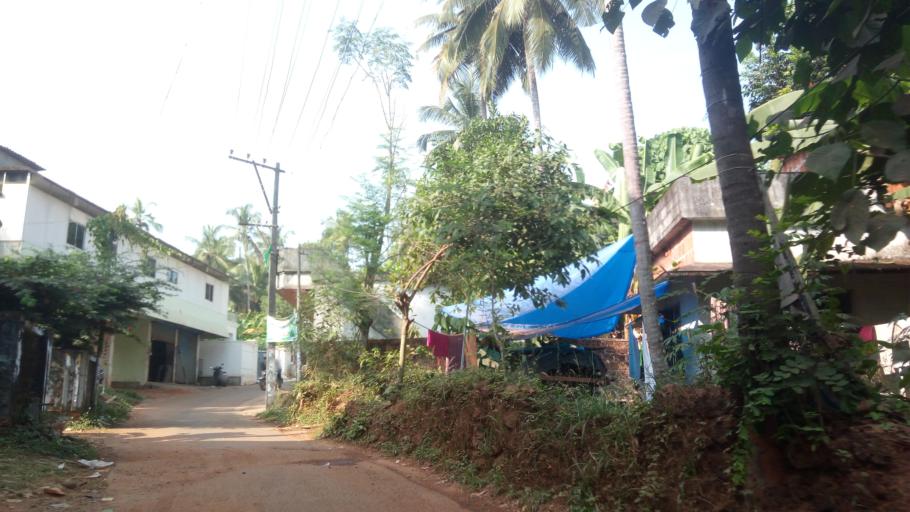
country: IN
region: Kerala
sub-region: Malappuram
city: Malappuram
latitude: 10.9959
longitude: 75.9998
